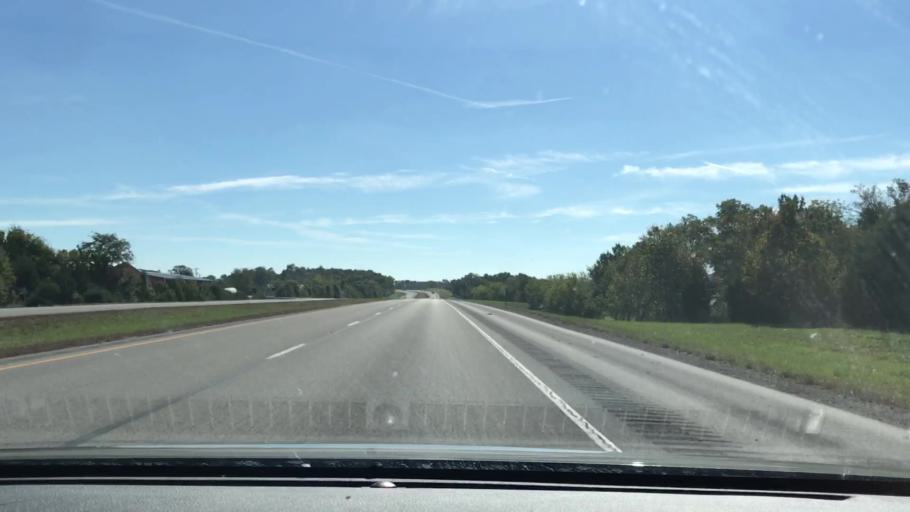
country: US
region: Kentucky
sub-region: Todd County
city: Elkton
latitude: 36.8333
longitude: -87.2322
